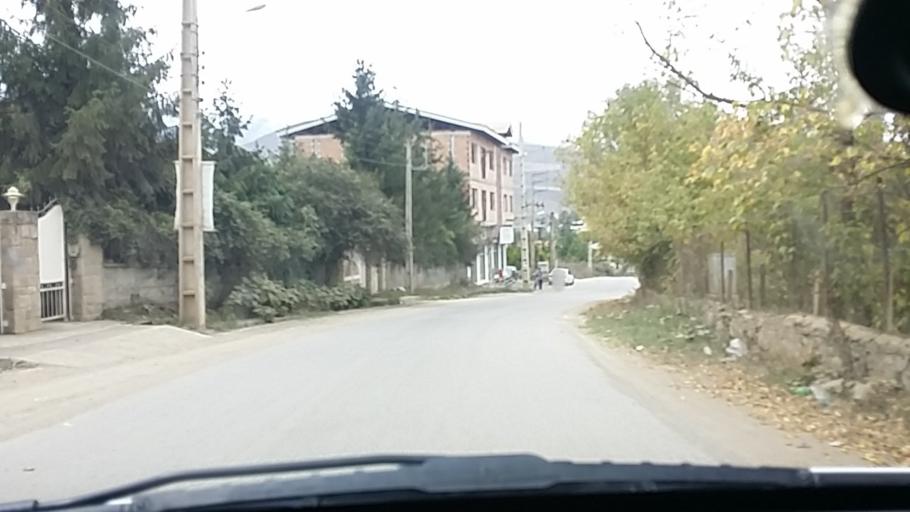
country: IR
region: Mazandaran
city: `Abbasabad
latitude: 36.4975
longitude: 51.1642
